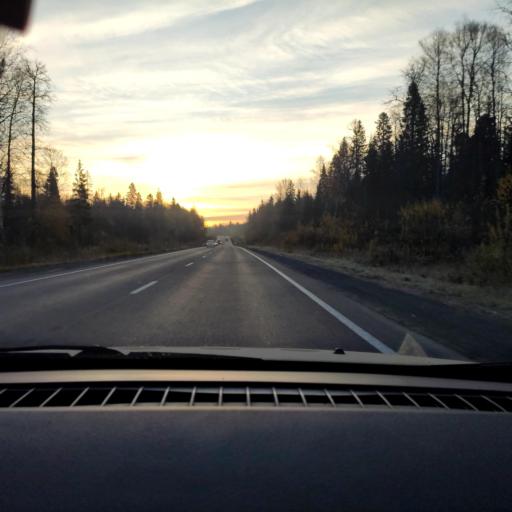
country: RU
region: Perm
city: Novyye Lyady
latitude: 58.0291
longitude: 56.4950
